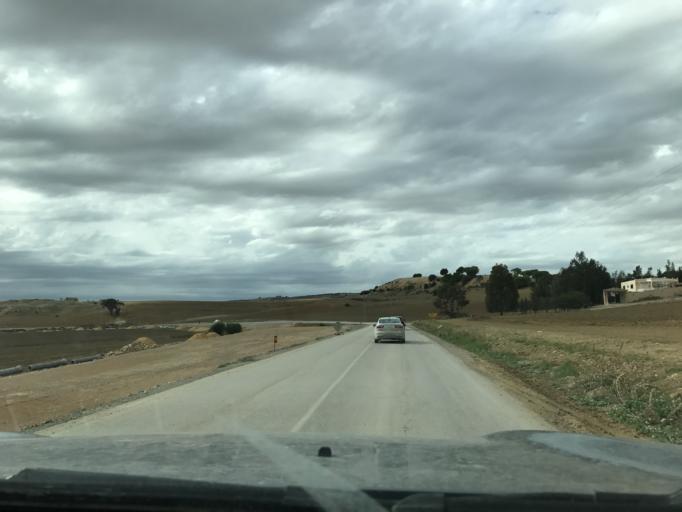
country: TN
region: Silyanah
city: Bu `Aradah
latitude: 36.1811
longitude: 9.6709
